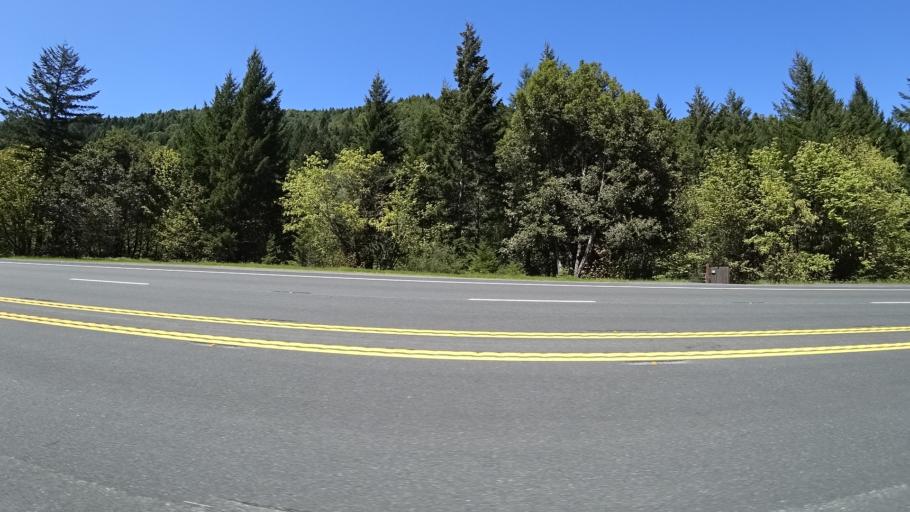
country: US
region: California
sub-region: Humboldt County
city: Willow Creek
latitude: 40.9146
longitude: -123.7036
